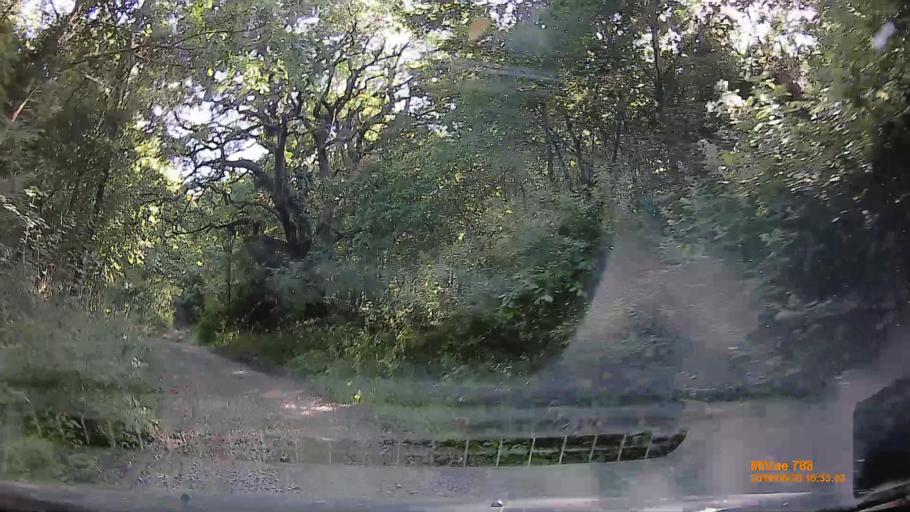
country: HU
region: Baranya
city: Buekkoesd
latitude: 46.1737
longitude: 18.0410
